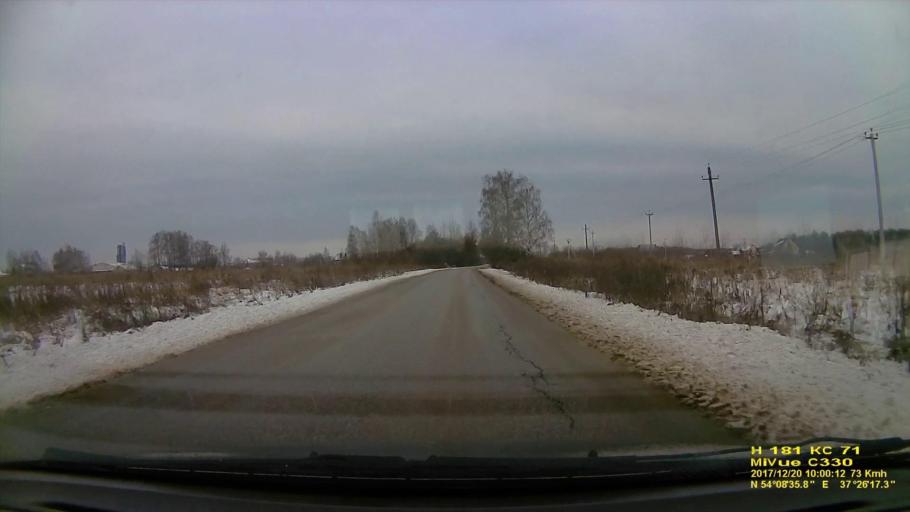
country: RU
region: Tula
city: Kosaya Gora
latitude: 54.1431
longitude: 37.4382
